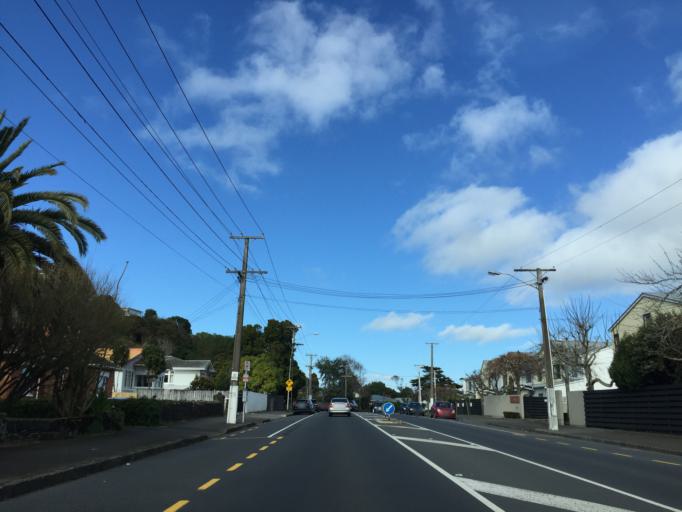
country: NZ
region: Auckland
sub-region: Auckland
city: Auckland
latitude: -36.9011
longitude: 174.7585
